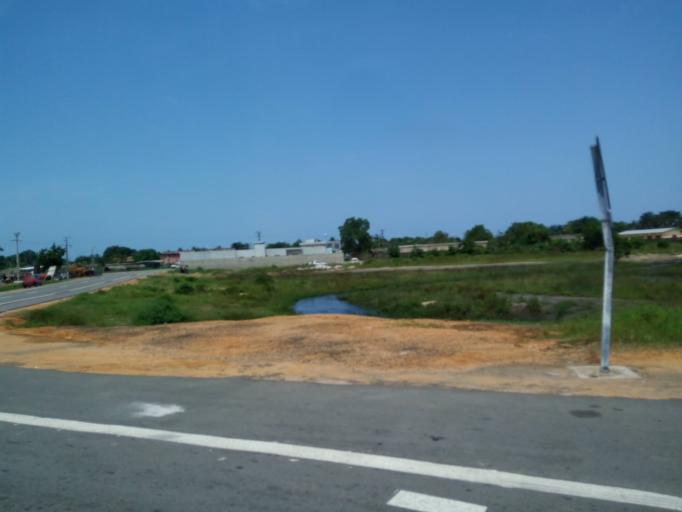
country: CI
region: Sud-Comoe
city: Grand-Bassam
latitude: 5.2235
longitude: -3.7286
